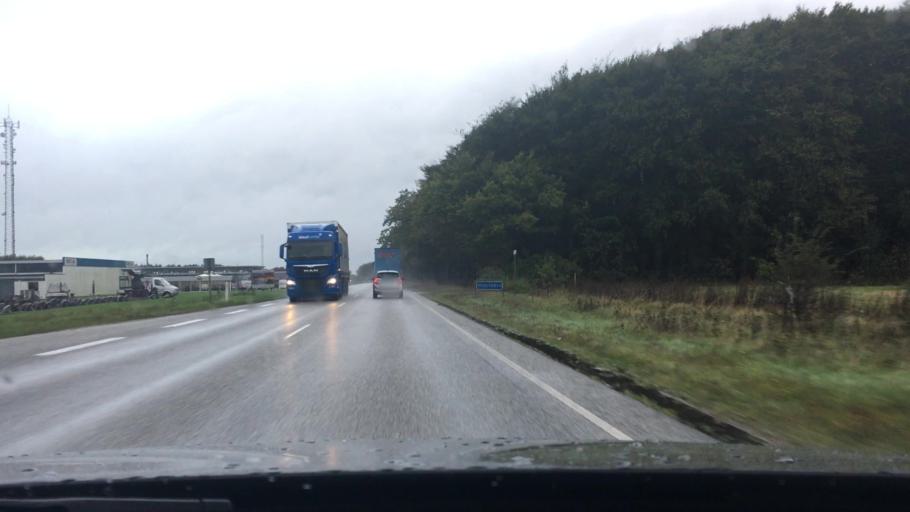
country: DK
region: Central Jutland
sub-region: Holstebro Kommune
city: Holstebro
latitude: 56.3396
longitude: 8.6413
